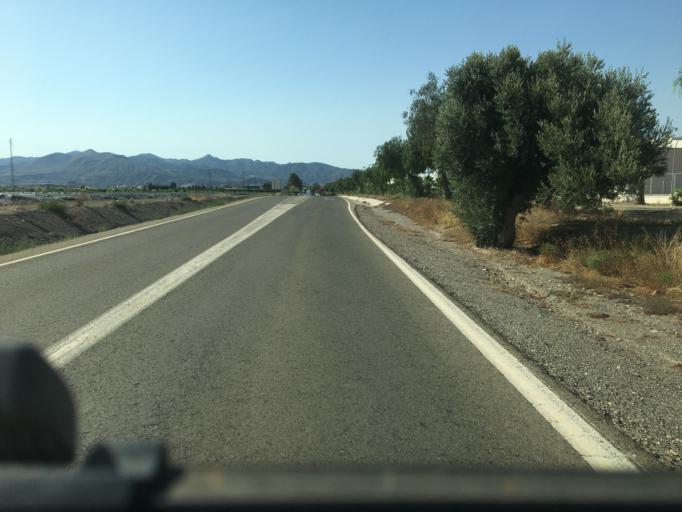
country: ES
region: Andalusia
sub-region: Provincia de Almeria
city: Huercal-Overa
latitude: 37.4178
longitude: -1.9678
